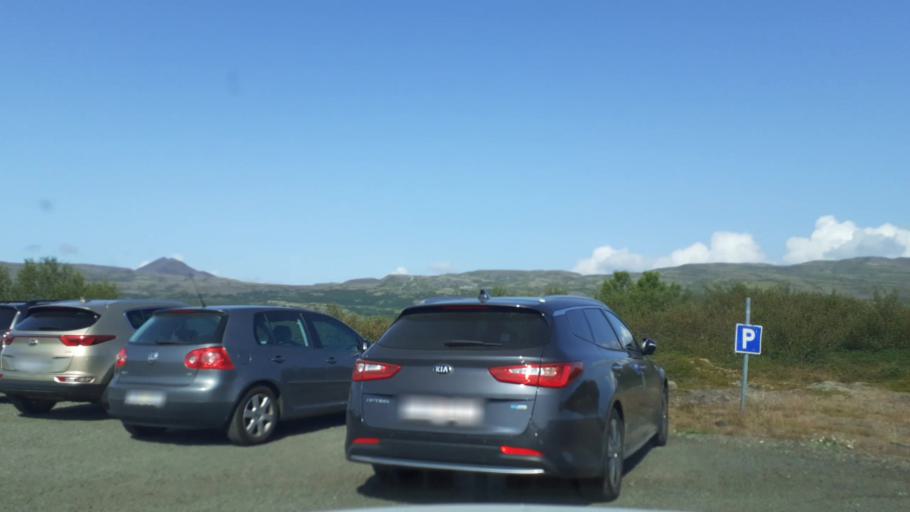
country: IS
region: West
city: Borgarnes
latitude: 64.7560
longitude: -21.5480
